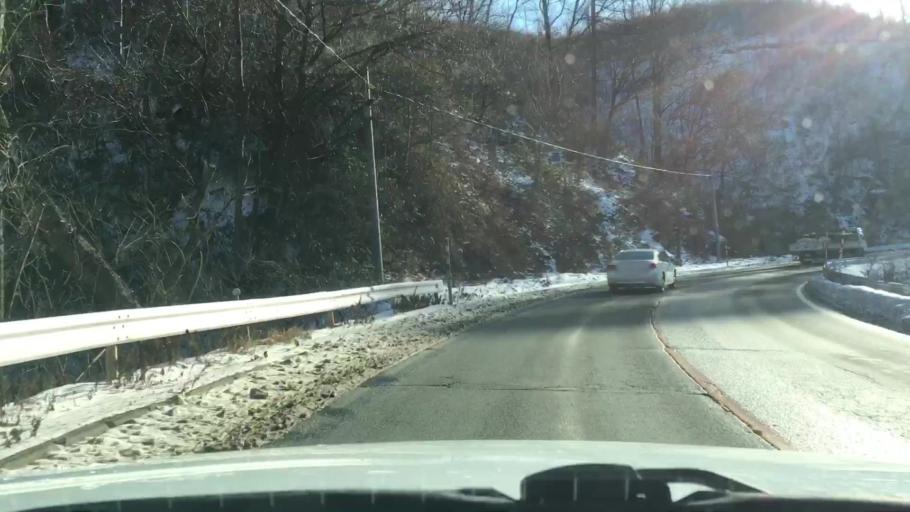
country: JP
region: Iwate
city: Morioka-shi
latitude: 39.6605
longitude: 141.3366
